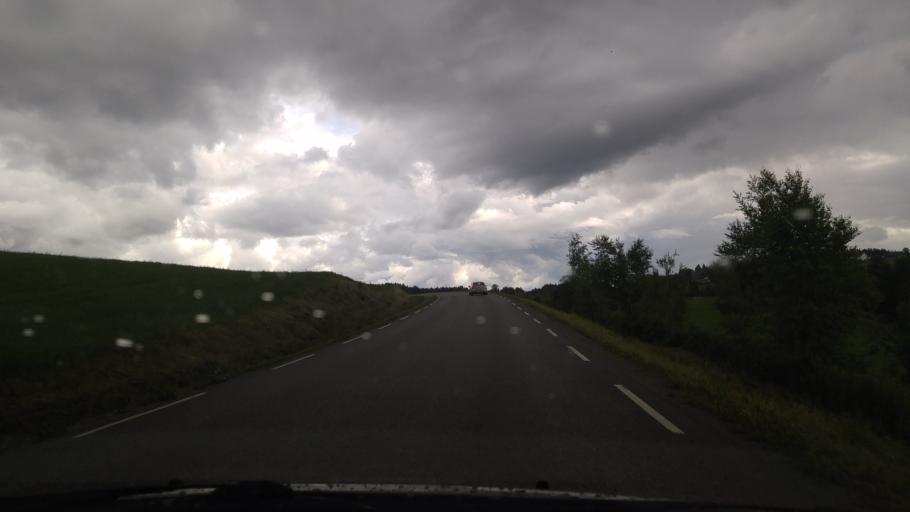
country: NO
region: Nord-Trondelag
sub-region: Levanger
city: Skogn
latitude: 63.6633
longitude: 11.2371
